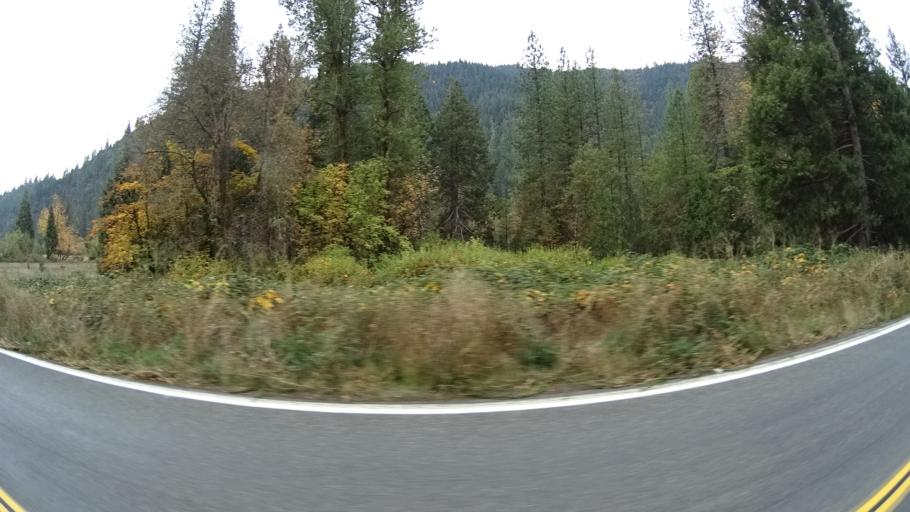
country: US
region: California
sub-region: Siskiyou County
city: Happy Camp
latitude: 41.8763
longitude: -123.4169
